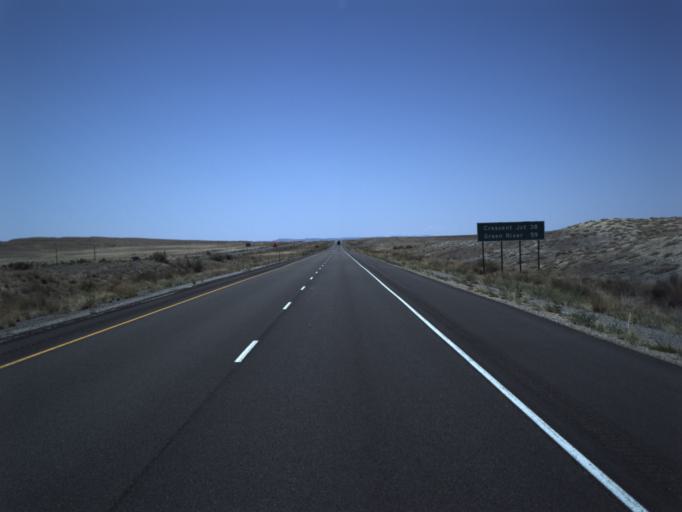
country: US
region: Colorado
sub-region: Mesa County
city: Loma
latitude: 39.1045
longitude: -109.1964
